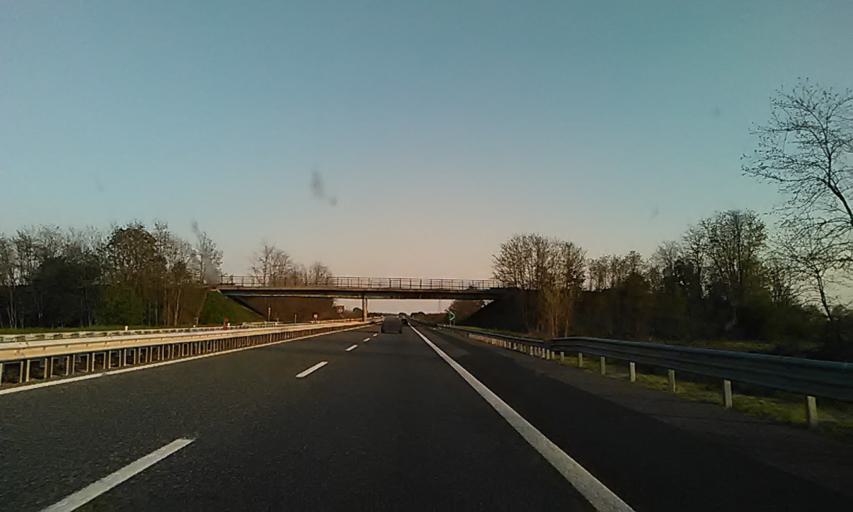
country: IT
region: Piedmont
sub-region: Provincia di Novara
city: Carpignano Sesia
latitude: 45.5473
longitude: 8.4243
